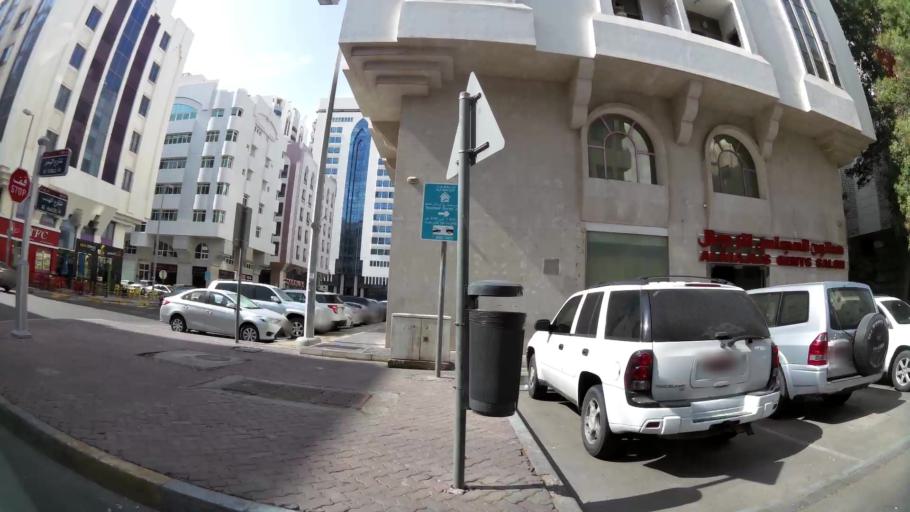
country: AE
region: Abu Dhabi
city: Abu Dhabi
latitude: 24.4747
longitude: 54.3524
